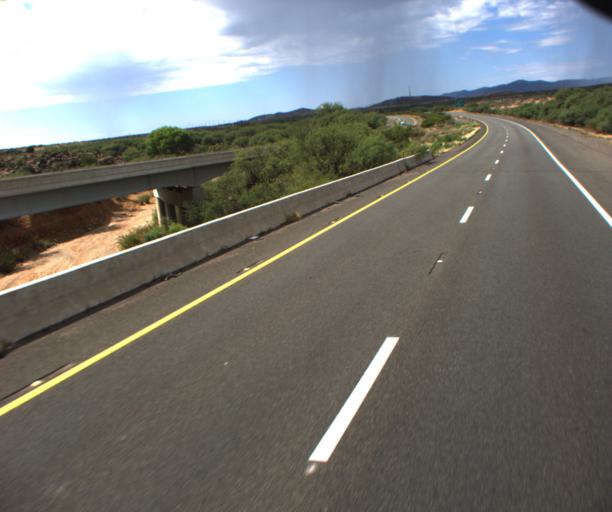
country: US
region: Arizona
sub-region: Yavapai County
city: Spring Valley
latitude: 34.3671
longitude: -112.1141
